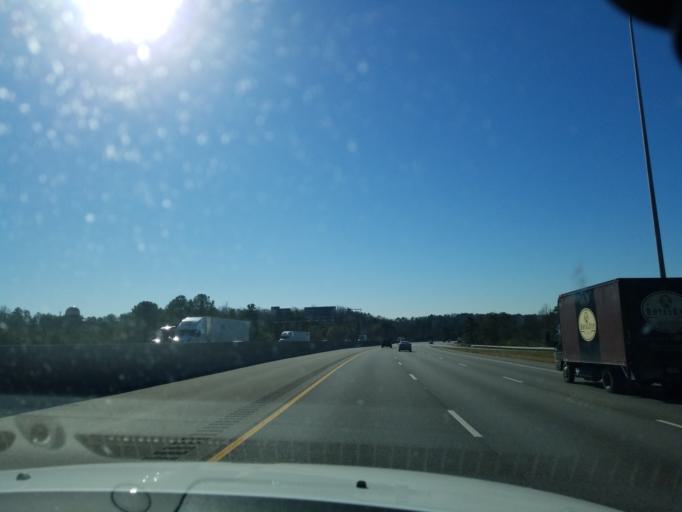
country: US
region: Alabama
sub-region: Jefferson County
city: Irondale
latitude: 33.5401
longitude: -86.6441
